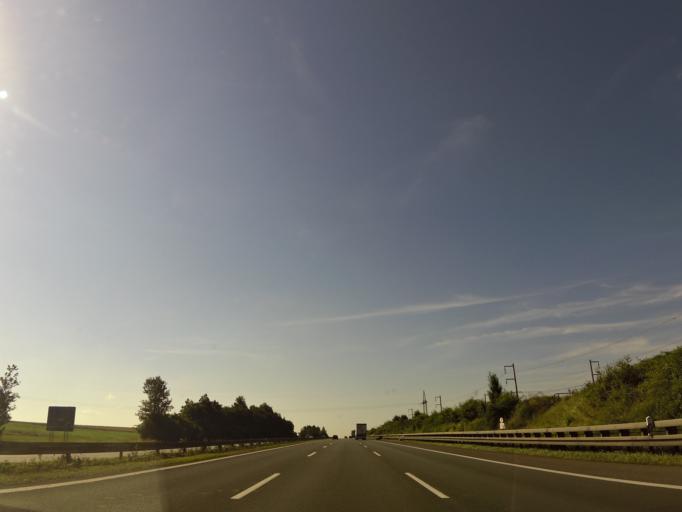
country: DE
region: Bavaria
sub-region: Regierungsbezirk Mittelfranken
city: Allersberg
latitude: 49.2018
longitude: 11.2392
